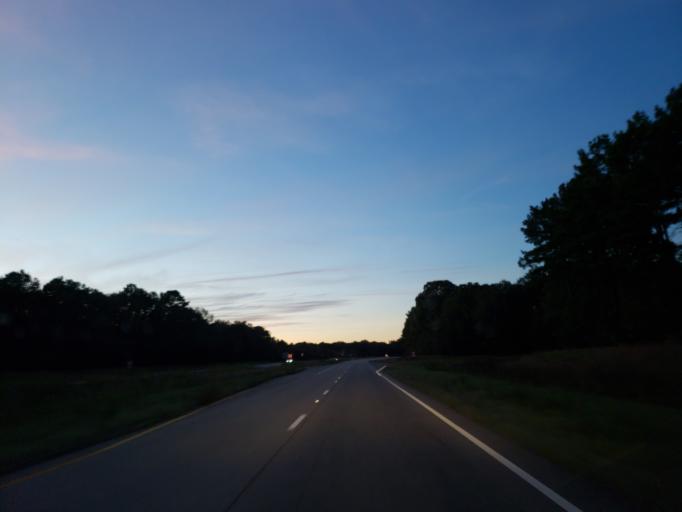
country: US
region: Mississippi
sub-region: Wayne County
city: Waynesboro
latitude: 31.8461
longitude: -88.7130
